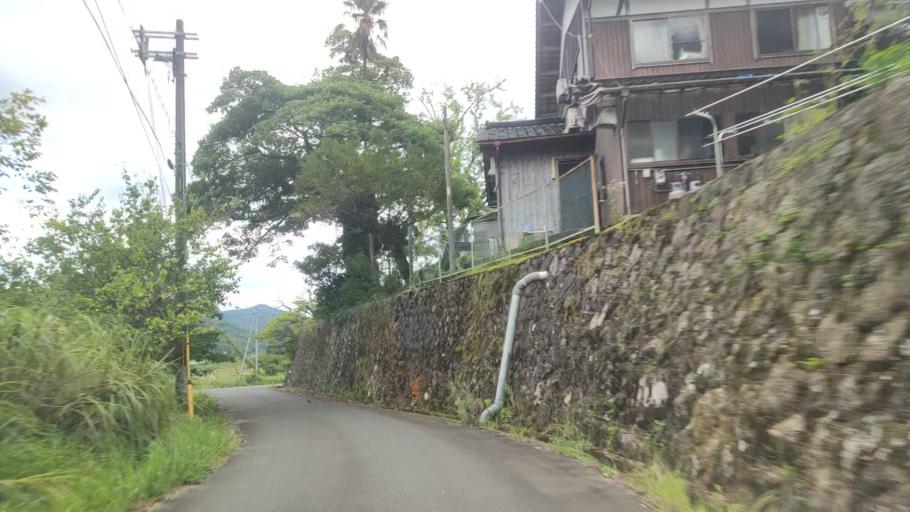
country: JP
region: Hyogo
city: Toyooka
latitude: 35.5992
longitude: 134.8812
